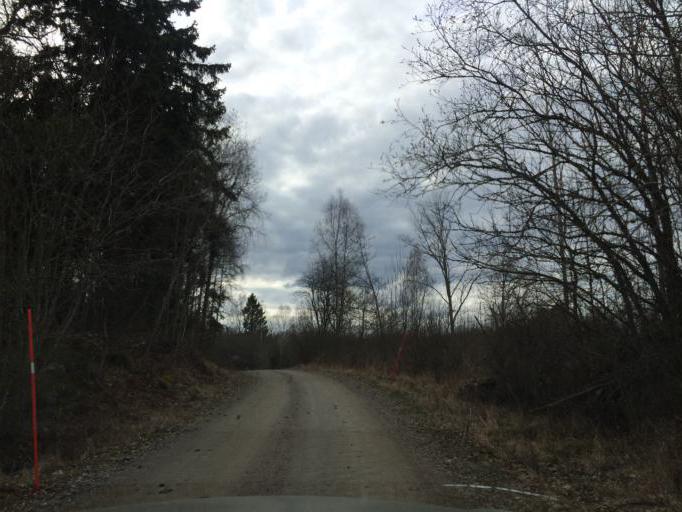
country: SE
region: Soedermanland
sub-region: Eskilstuna Kommun
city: Hallbybrunn
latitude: 59.4175
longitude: 16.3947
